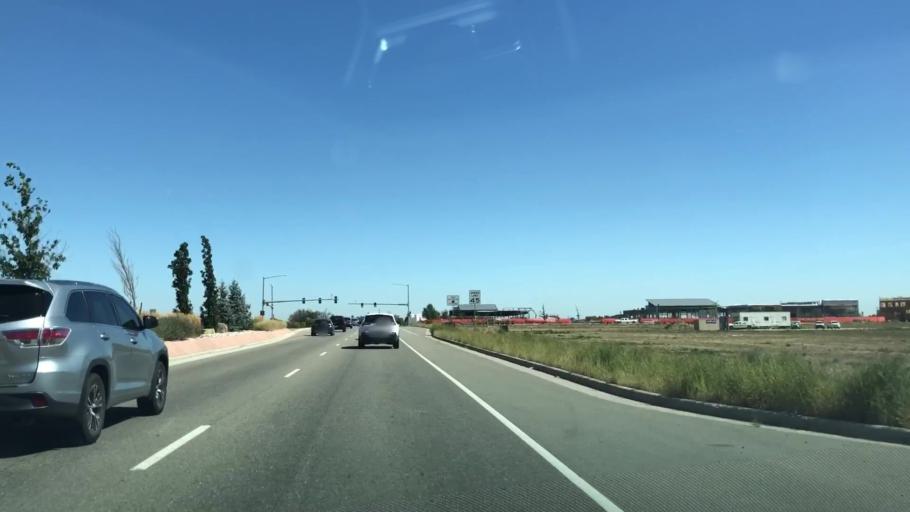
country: US
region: Colorado
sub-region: Weld County
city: Windsor
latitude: 40.5229
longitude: -104.9795
